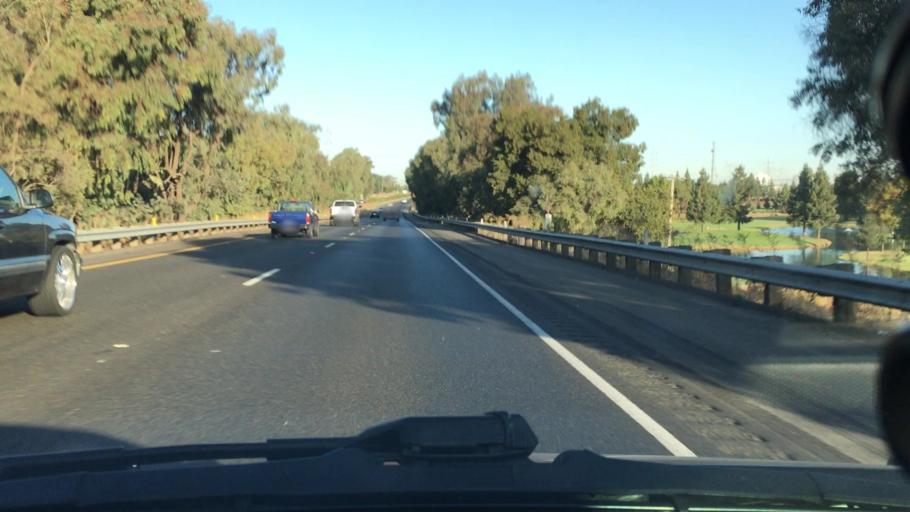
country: US
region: California
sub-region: Sacramento County
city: Elk Grove
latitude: 38.3642
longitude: -121.3491
